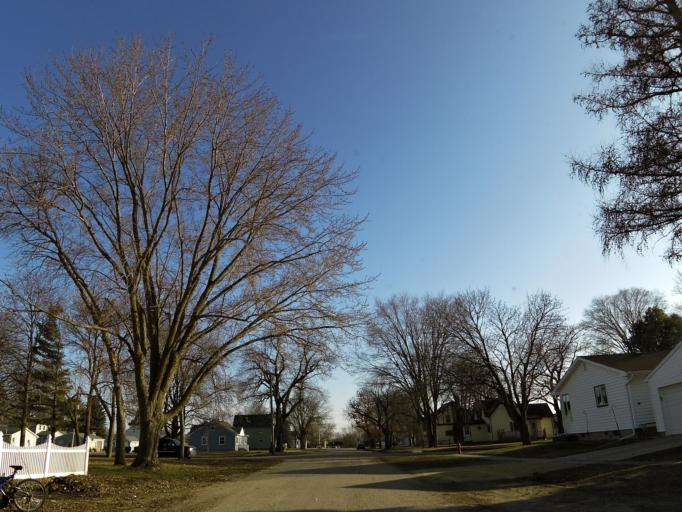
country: US
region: Iowa
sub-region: Worth County
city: Northwood
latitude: 43.4468
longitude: -93.2235
